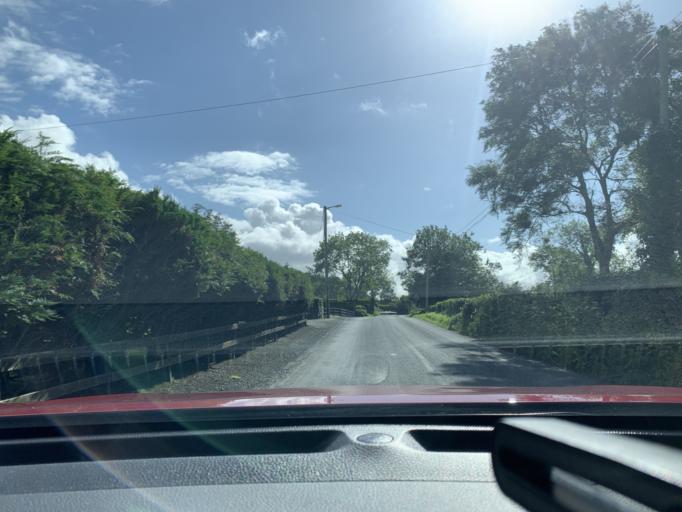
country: IE
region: Connaught
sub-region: Sligo
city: Strandhill
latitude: 54.3390
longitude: -8.5409
